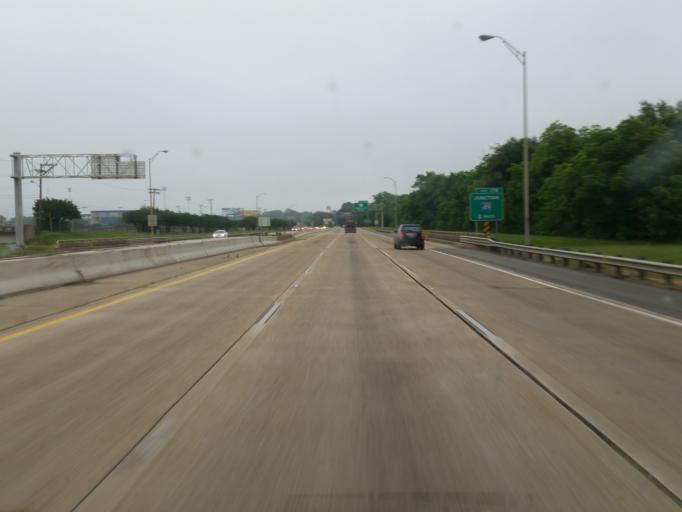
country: US
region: Louisiana
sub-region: Caddo Parish
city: Shreveport
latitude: 32.4743
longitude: -93.7895
